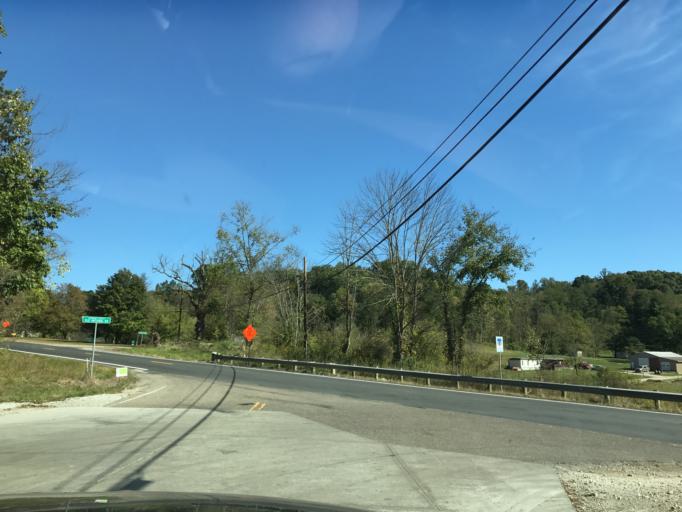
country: US
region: Ohio
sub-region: Guernsey County
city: Byesville
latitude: 40.0238
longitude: -81.5094
